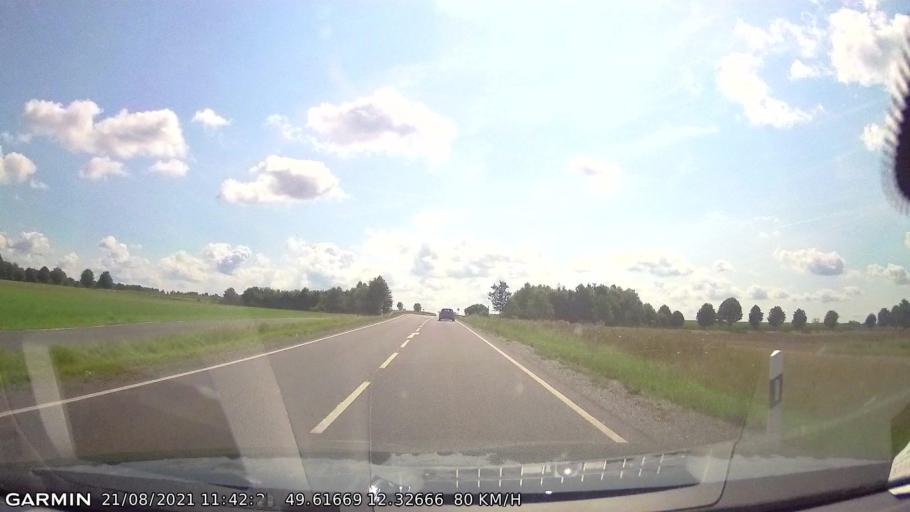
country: DE
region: Bavaria
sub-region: Upper Palatinate
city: Vohenstrauss
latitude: 49.6167
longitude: 12.3266
